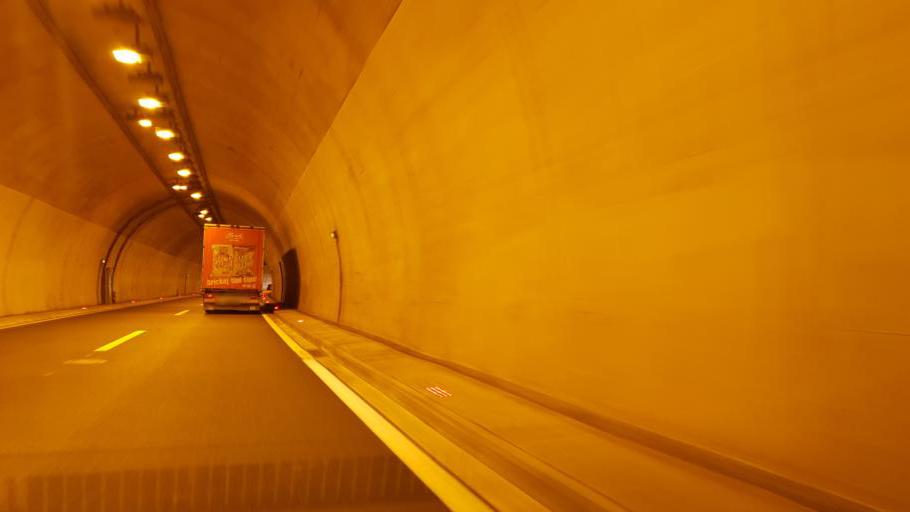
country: HR
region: Primorsko-Goranska
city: Matulji
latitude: 45.3777
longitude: 14.3168
